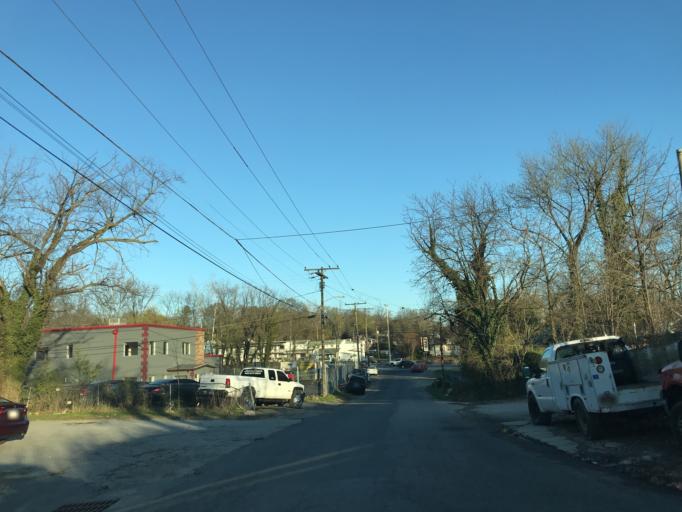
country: US
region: Maryland
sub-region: Baltimore County
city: Rosedale
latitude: 39.3179
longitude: -76.5171
